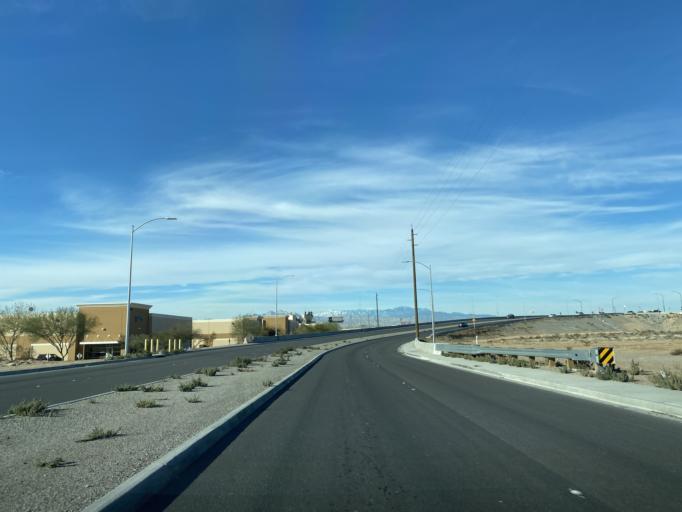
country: US
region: Nevada
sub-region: Clark County
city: Nellis Air Force Base
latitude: 36.2696
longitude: -115.0532
